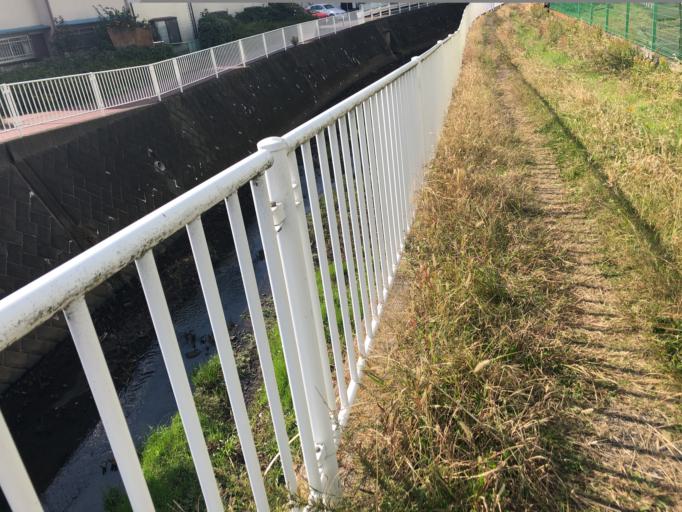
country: JP
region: Tokyo
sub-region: Machida-shi
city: Machida
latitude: 35.5271
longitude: 139.4977
